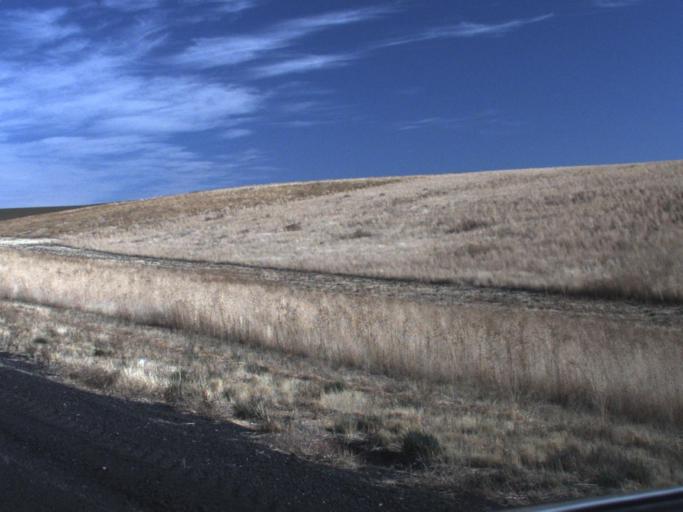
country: US
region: Washington
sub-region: Adams County
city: Ritzville
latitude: 47.1441
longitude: -118.6869
